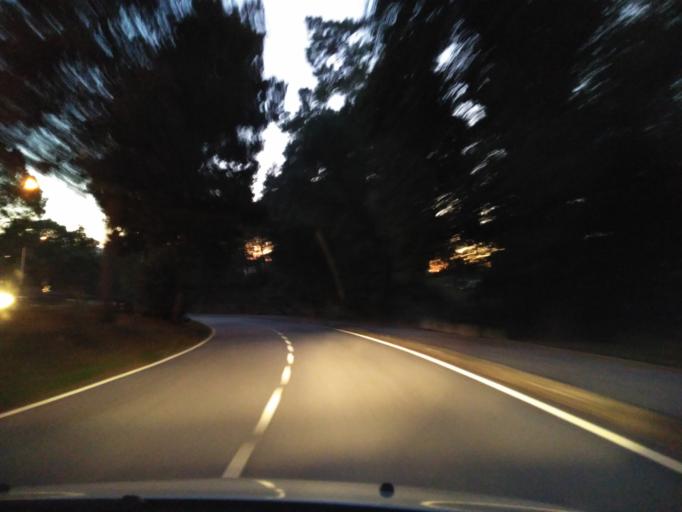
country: PT
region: Braga
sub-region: Braga
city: Braga
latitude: 41.5578
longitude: -8.3932
